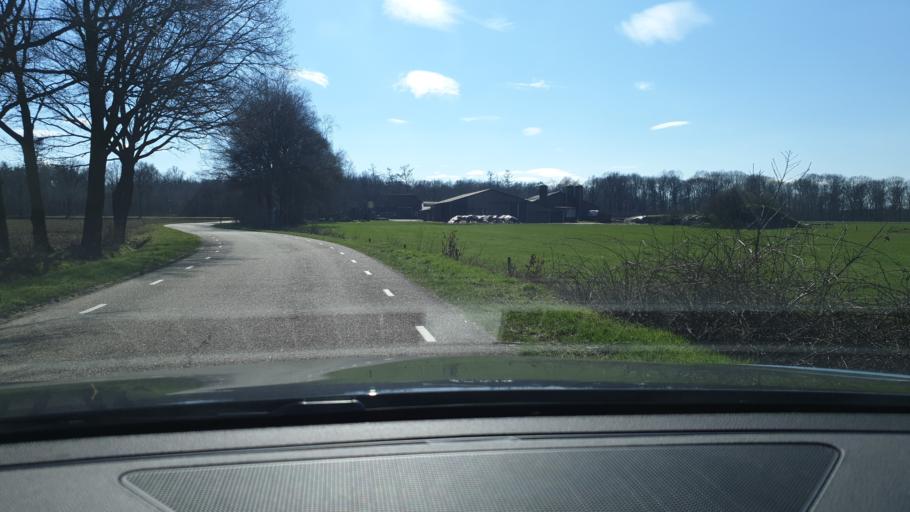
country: NL
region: North Brabant
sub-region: Gemeente Oirschot
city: Oostelbeers
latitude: 51.4523
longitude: 5.2968
